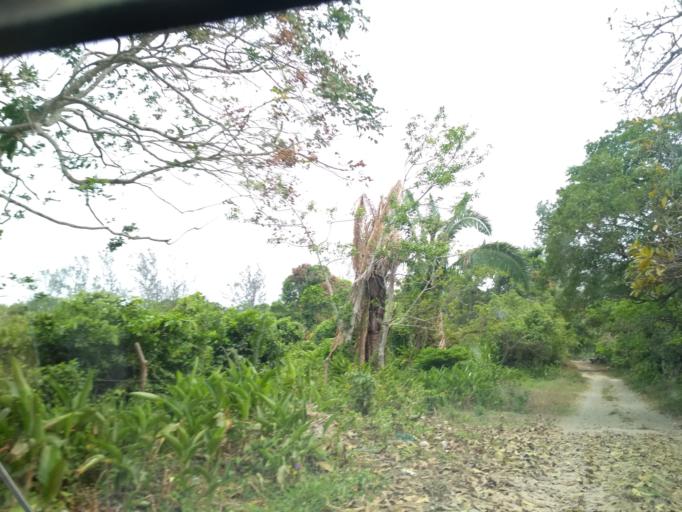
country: MX
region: Veracruz
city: Anton Lizardo
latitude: 19.0128
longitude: -95.9887
